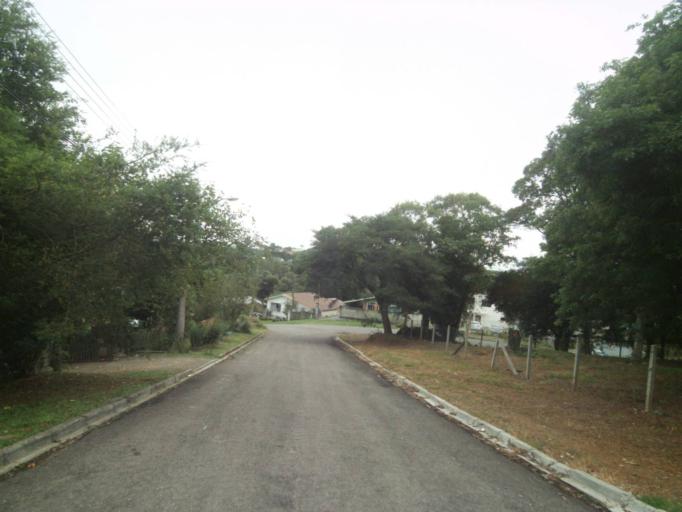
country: BR
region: Parana
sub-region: Curitiba
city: Curitiba
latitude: -25.4013
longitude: -49.2997
